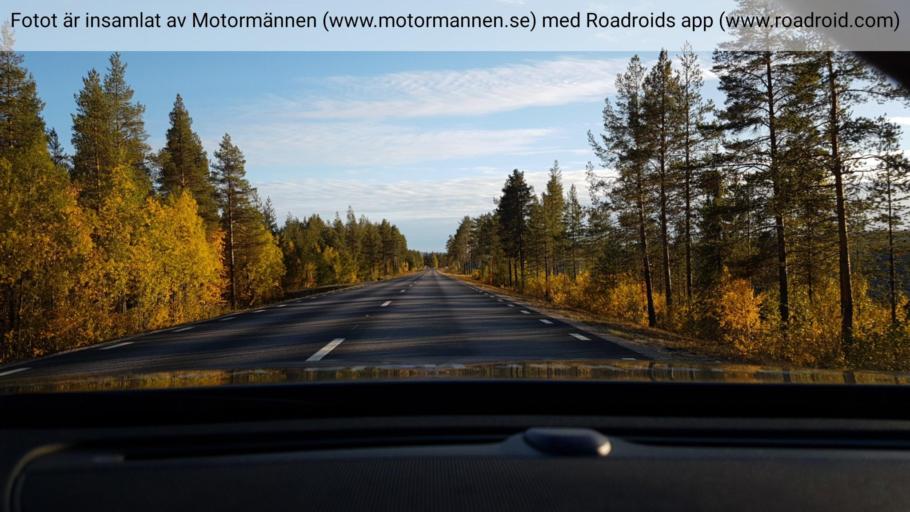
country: SE
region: Norrbotten
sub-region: Jokkmokks Kommun
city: Jokkmokk
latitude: 66.6367
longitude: 19.8242
